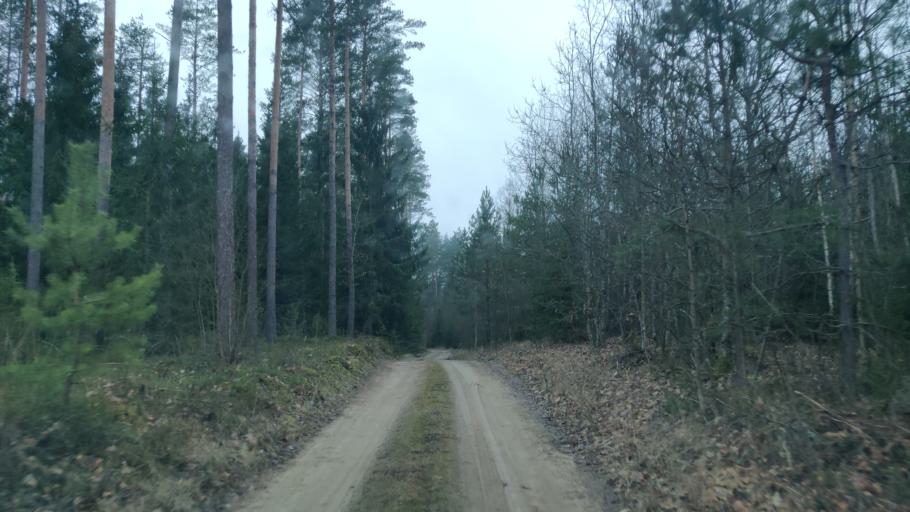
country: LT
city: Trakai
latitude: 54.5570
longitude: 24.9545
